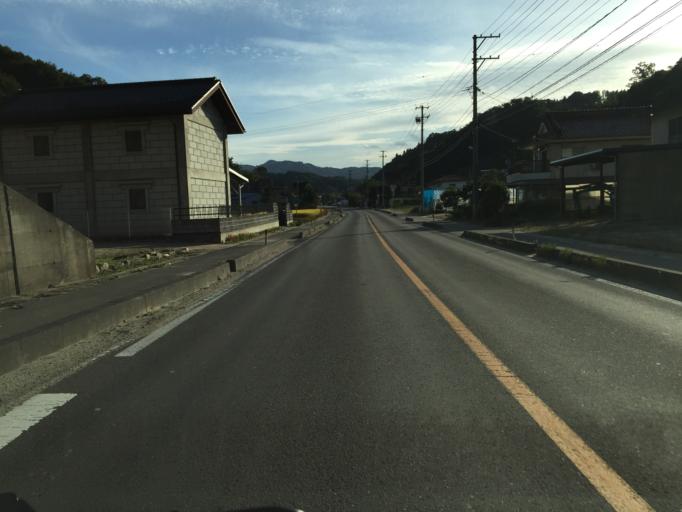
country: JP
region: Fukushima
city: Hobaramachi
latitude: 37.6764
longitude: 140.6153
